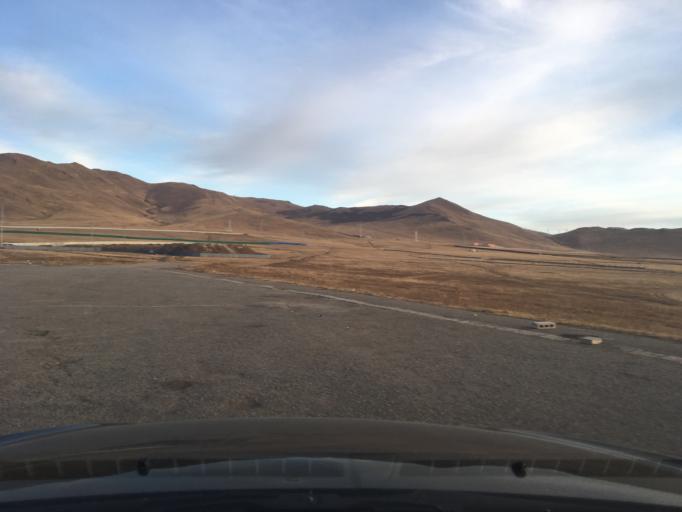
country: MN
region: Ulaanbaatar
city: Ulaanbaatar
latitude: 47.8448
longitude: 106.7951
